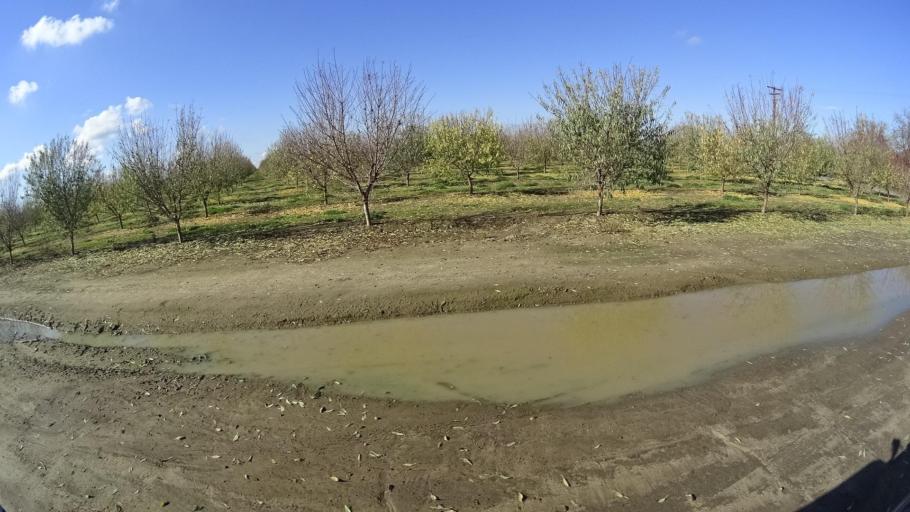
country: US
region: California
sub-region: Kern County
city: McFarland
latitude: 35.7029
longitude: -119.2586
